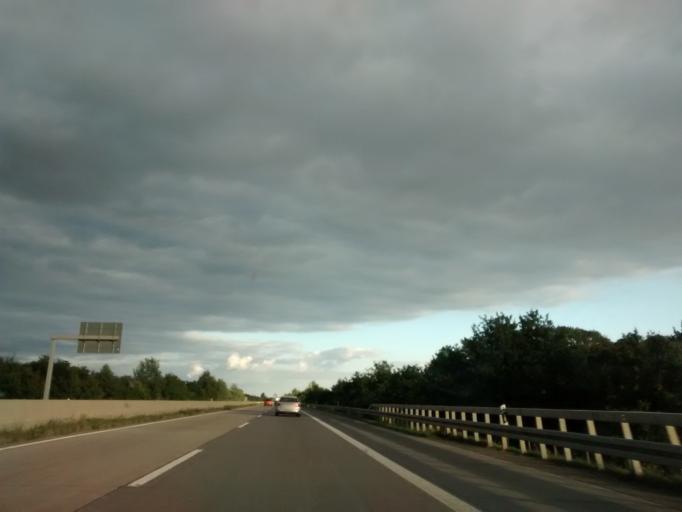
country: DE
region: North Rhine-Westphalia
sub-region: Regierungsbezirk Munster
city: Rheine
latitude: 52.3166
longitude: 7.4487
